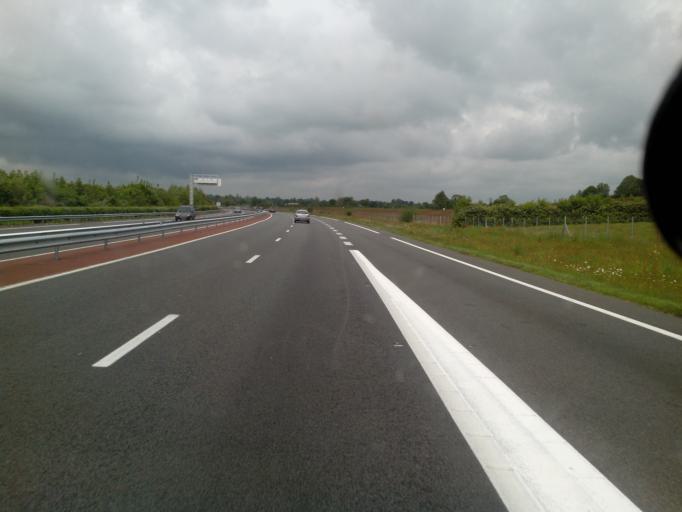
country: FR
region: Lower Normandy
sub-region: Departement de la Manche
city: Saint-Senier-sous-Avranches
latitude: 48.7452
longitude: -1.2845
